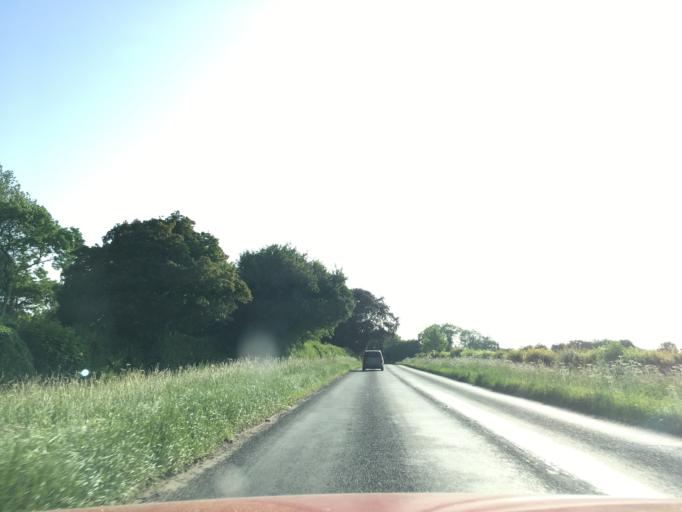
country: GB
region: England
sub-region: Gloucestershire
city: Fairford
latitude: 51.7033
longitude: -1.8121
